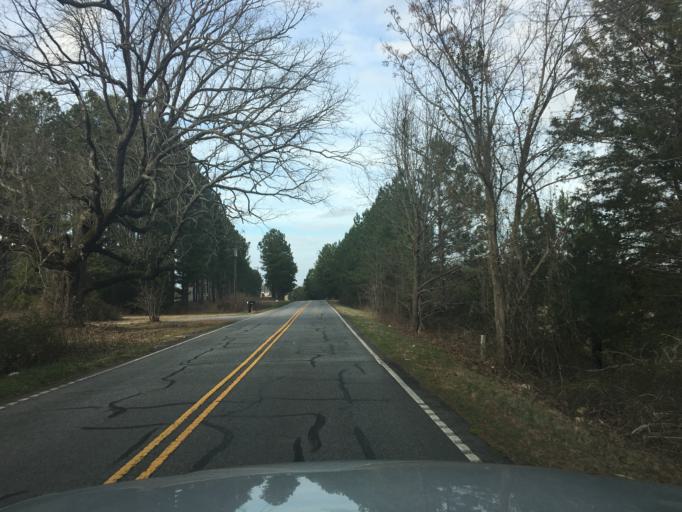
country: US
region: South Carolina
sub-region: Abbeville County
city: Lake Secession
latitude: 34.3679
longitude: -82.5201
